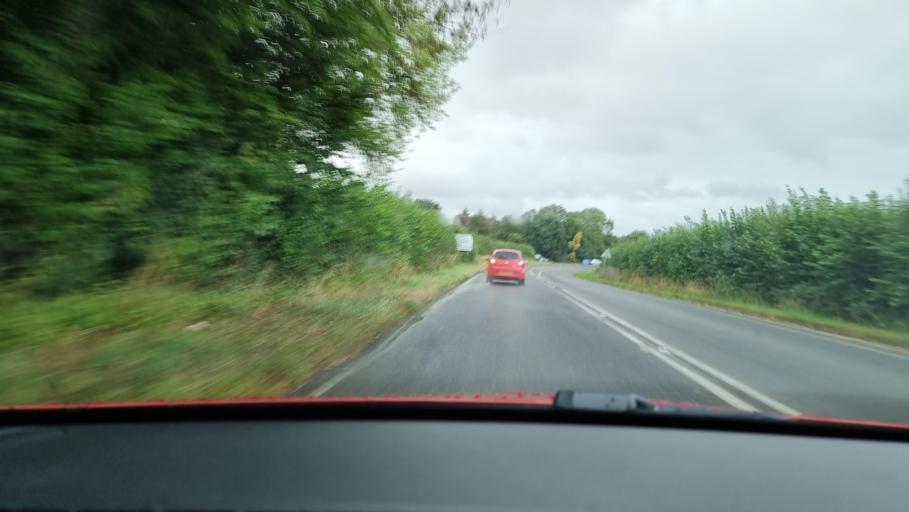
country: GB
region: England
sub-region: Buckinghamshire
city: Chesham
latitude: 51.7205
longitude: -0.5802
